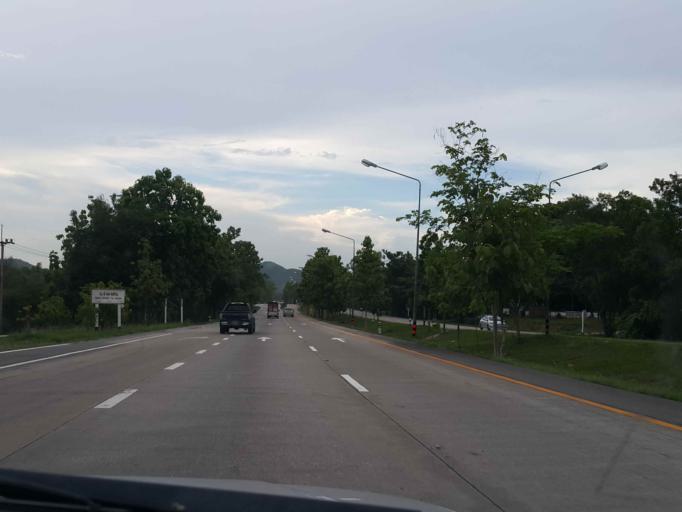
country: TH
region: Lamphun
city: Mae Tha
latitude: 18.4664
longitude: 99.1277
